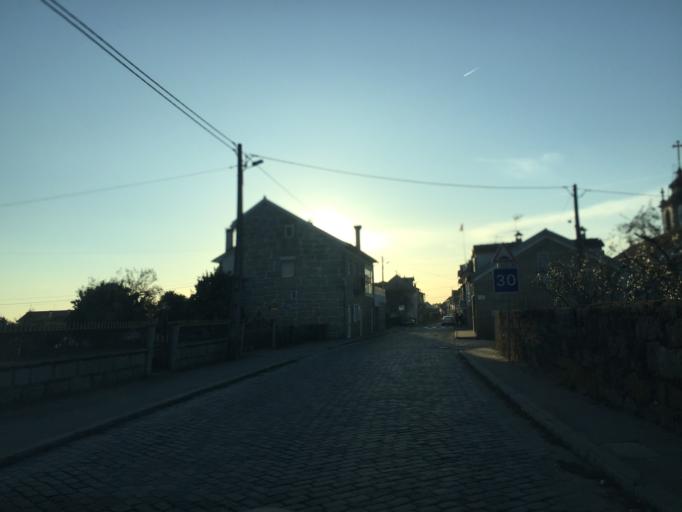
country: PT
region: Viseu
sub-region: Concelho de Carregal do Sal
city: Carregal do Sal
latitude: 40.4590
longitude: -7.9437
